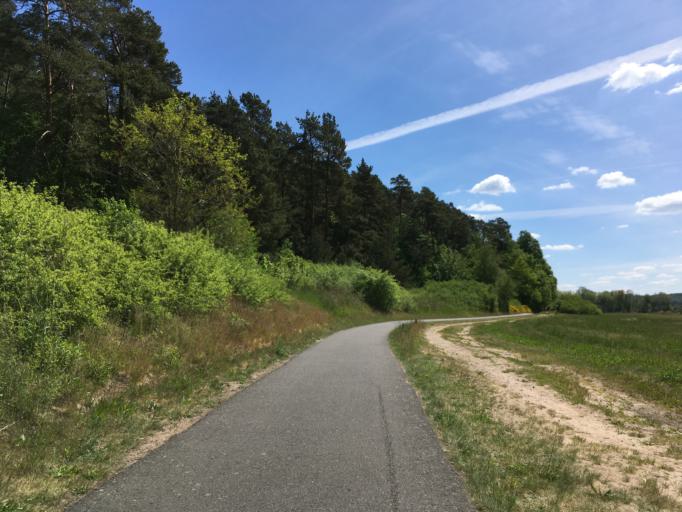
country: DE
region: Brandenburg
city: Niederfinow
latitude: 52.8482
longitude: 13.8872
